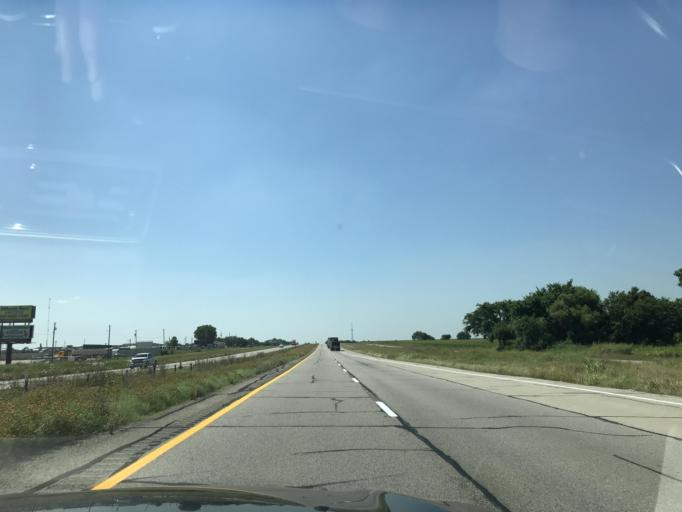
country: US
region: Texas
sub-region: Johnson County
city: Alvarado
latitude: 32.3467
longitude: -97.1944
